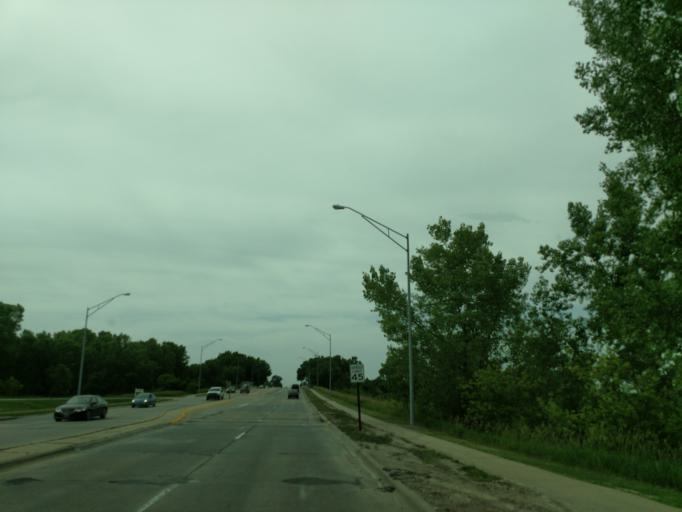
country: US
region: Nebraska
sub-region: Douglas County
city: Ralston
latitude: 41.1903
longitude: -96.0621
